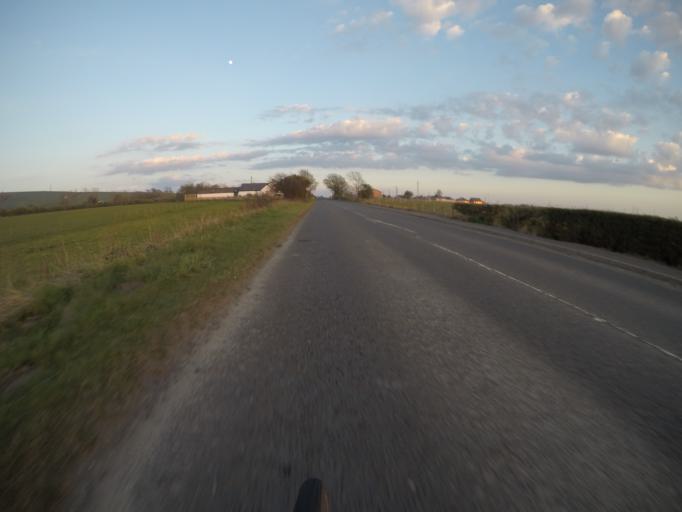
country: GB
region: Scotland
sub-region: South Ayrshire
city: Troon
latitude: 55.5607
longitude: -4.6317
